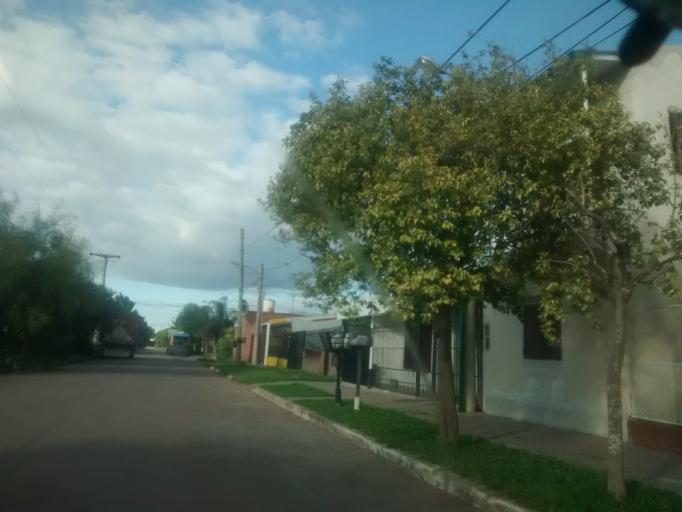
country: AR
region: Chaco
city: Fontana
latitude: -27.4520
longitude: -59.0259
